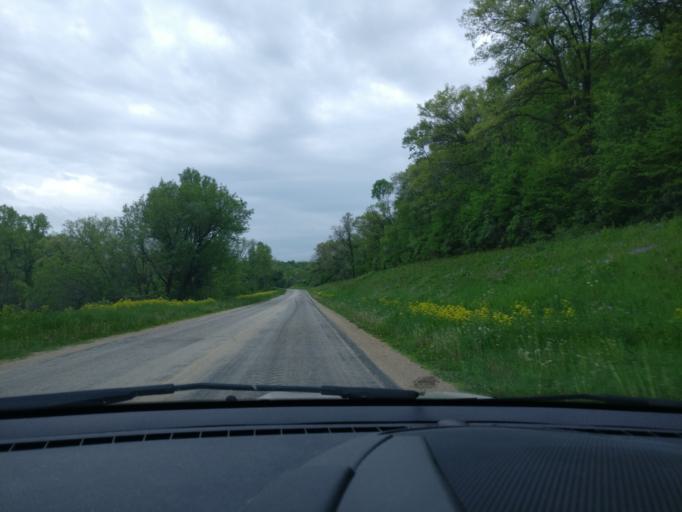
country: US
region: Wisconsin
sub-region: Lafayette County
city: Darlington
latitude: 42.7715
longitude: -90.0031
